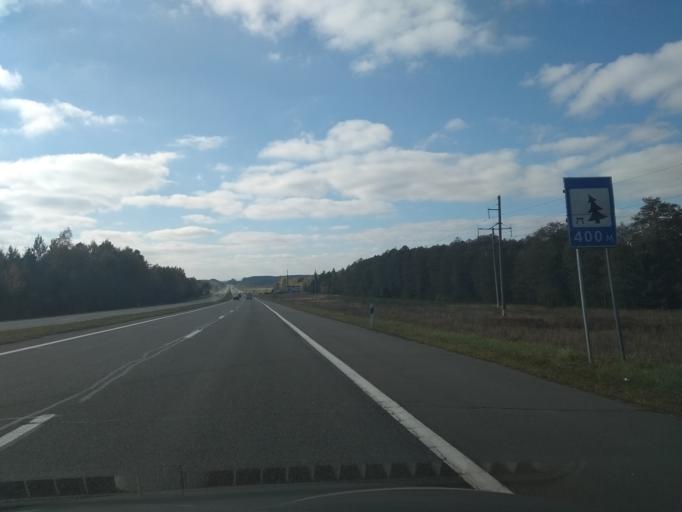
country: BY
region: Minsk
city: Stowbtsy
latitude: 53.5104
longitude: 26.6726
